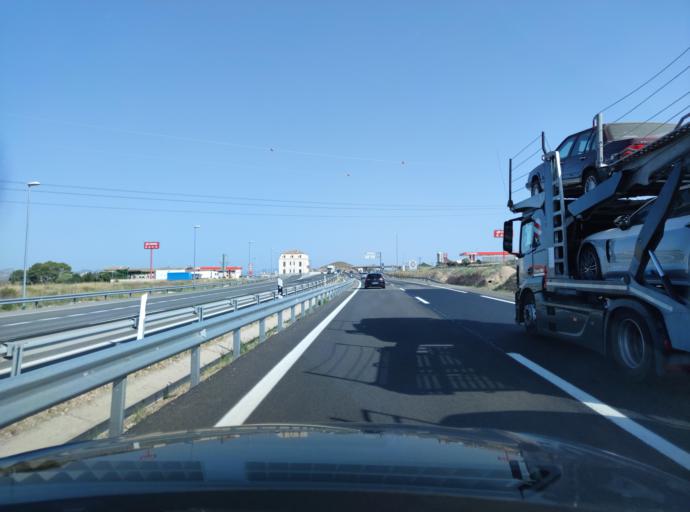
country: ES
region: Valencia
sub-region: Provincia de Alicante
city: Sax
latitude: 38.5713
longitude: -0.8380
